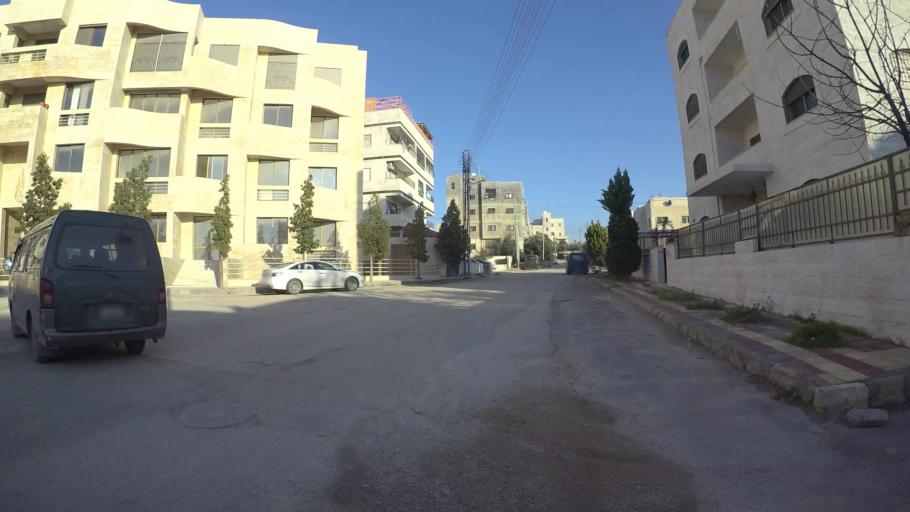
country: JO
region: Amman
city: Al Bunayyat ash Shamaliyah
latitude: 31.8984
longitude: 35.9055
